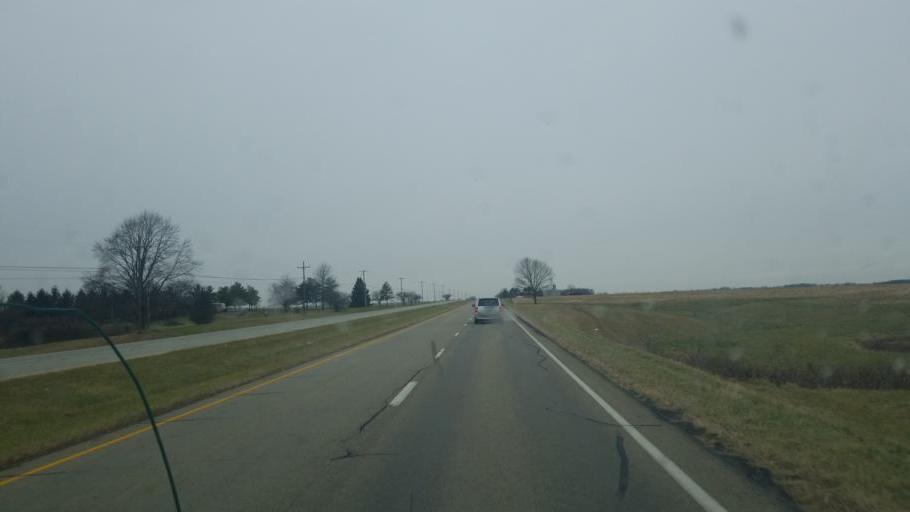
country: US
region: Indiana
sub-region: Henry County
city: Knightstown
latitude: 39.7929
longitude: -85.5713
